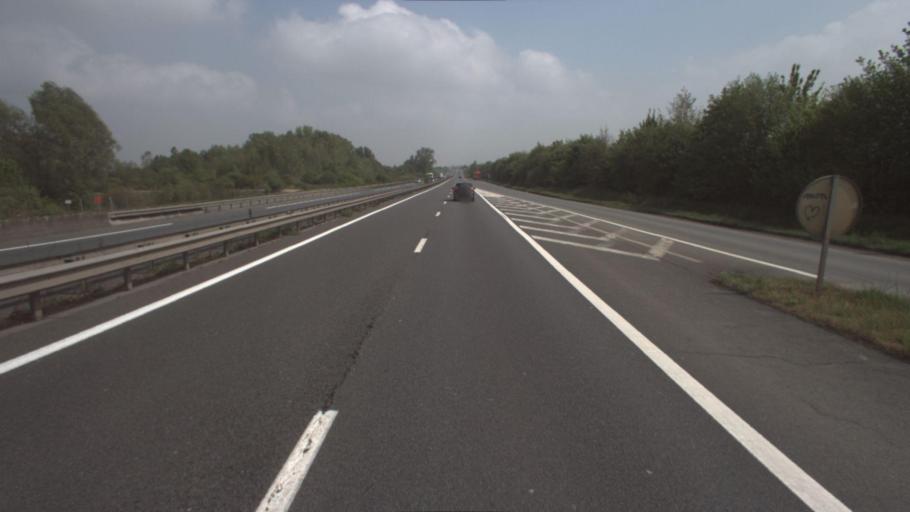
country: FR
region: Picardie
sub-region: Departement de l'Oise
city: Lagny-le-Sec
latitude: 49.0721
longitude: 2.7175
